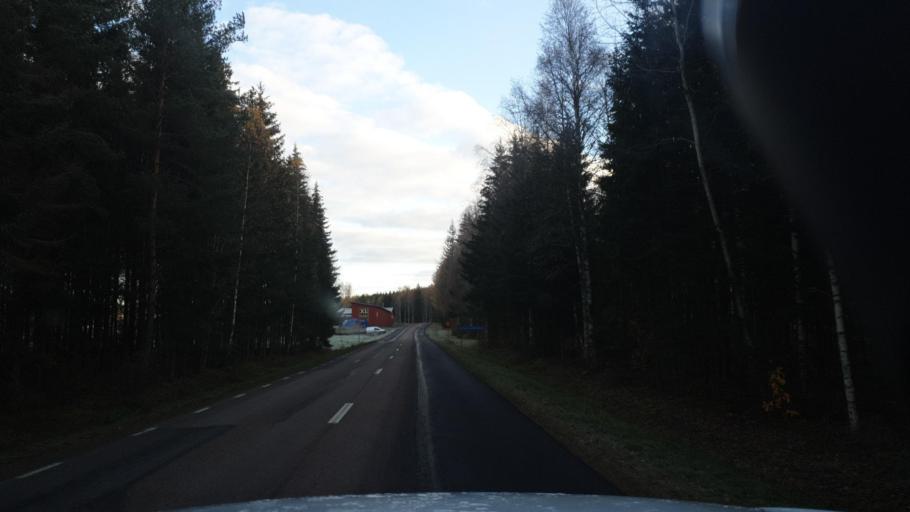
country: SE
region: Vaermland
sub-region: Eda Kommun
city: Amotfors
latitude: 59.7429
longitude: 12.2077
